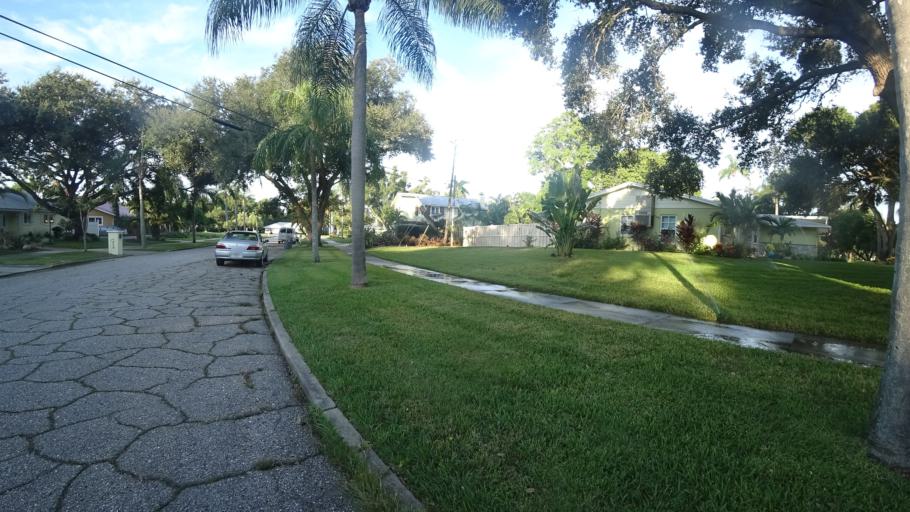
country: US
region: Florida
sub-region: Manatee County
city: Whitfield
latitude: 27.4070
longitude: -82.5717
